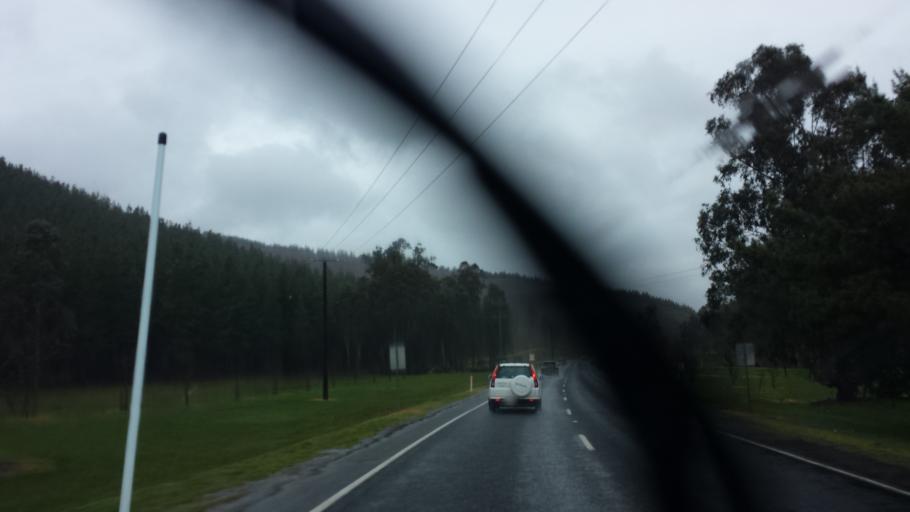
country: AU
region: Victoria
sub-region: Alpine
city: Mount Beauty
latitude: -36.5745
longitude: 146.7459
